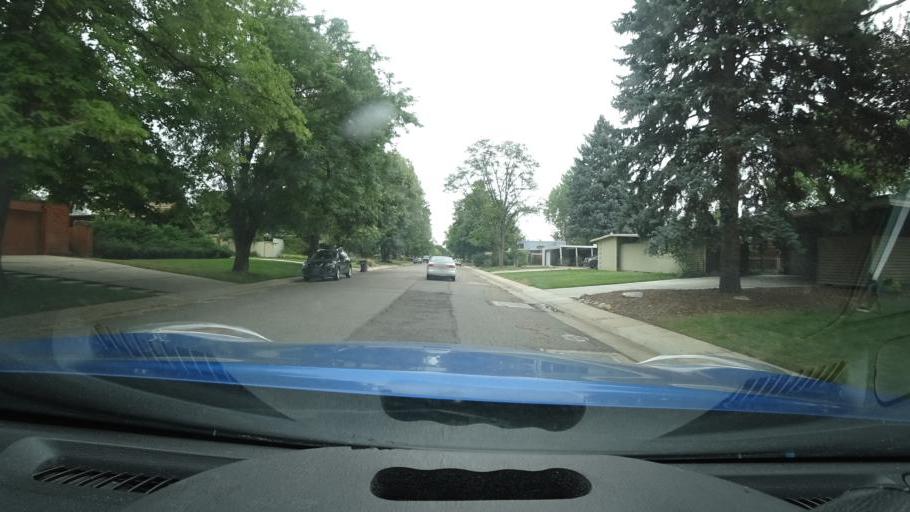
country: US
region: Colorado
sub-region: Arapahoe County
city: Glendale
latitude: 39.6844
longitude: -104.9183
